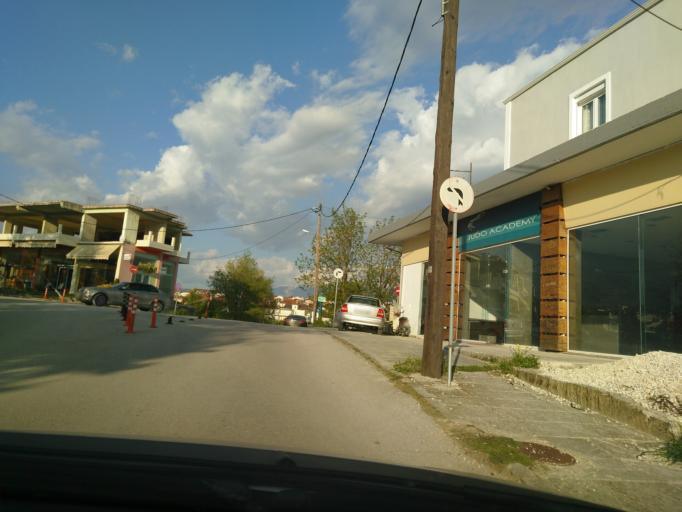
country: GR
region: Epirus
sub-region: Nomos Ioanninon
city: Anatoli
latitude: 39.6318
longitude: 20.8597
